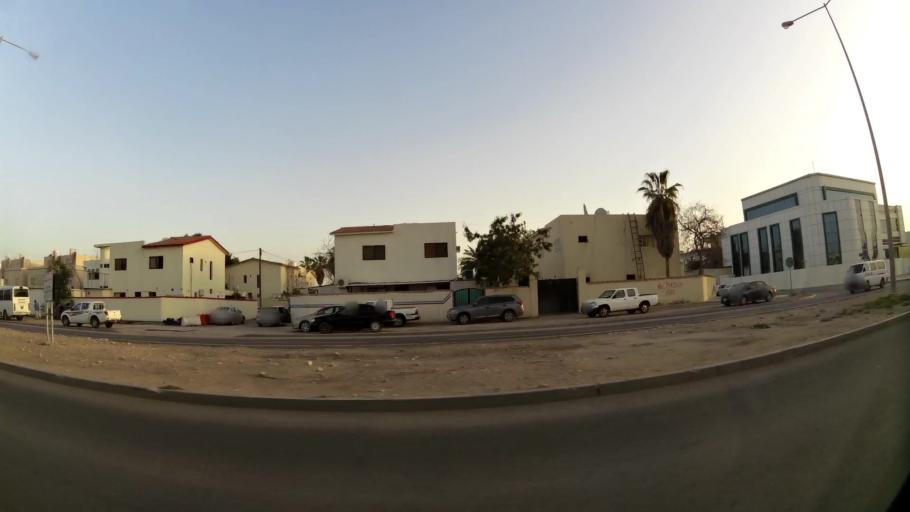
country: QA
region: Baladiyat ar Rayyan
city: Ar Rayyan
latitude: 25.3133
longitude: 51.4654
